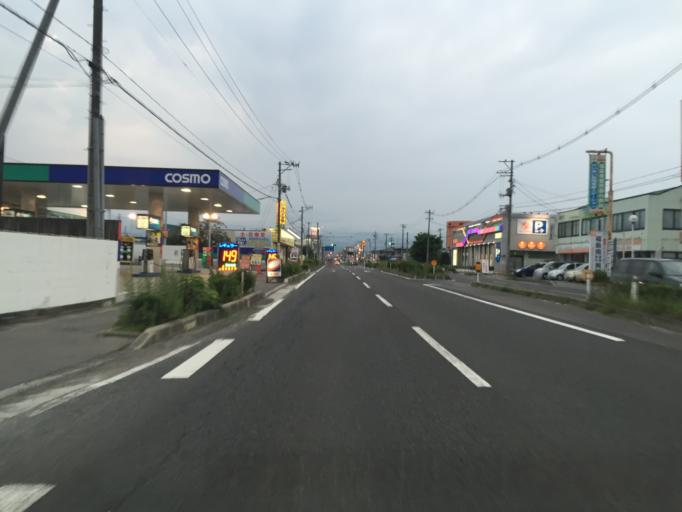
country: JP
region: Fukushima
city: Fukushima-shi
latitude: 37.7395
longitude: 140.4552
